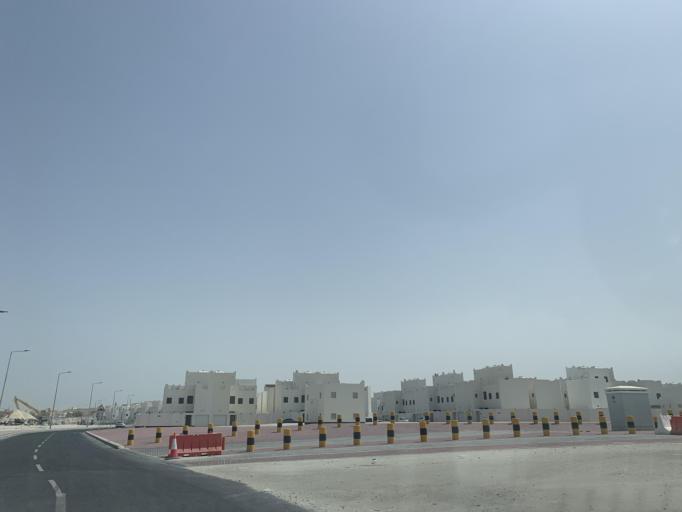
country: BH
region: Northern
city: Ar Rifa'
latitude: 26.1533
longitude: 50.5626
